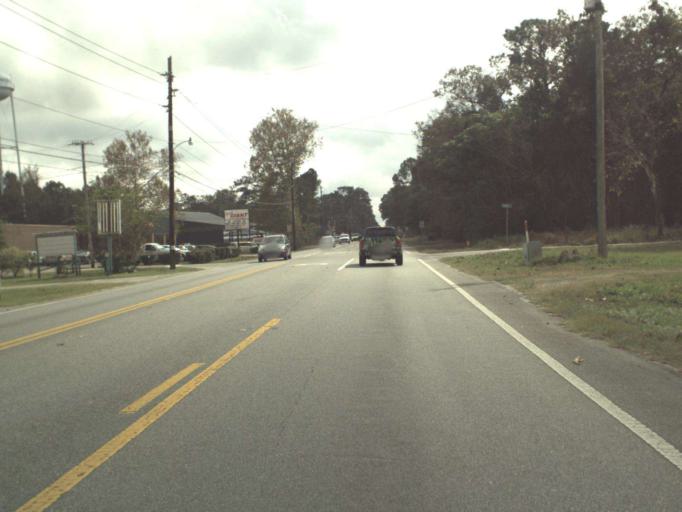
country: US
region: Florida
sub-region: Leon County
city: Woodville
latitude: 30.3183
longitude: -84.2484
